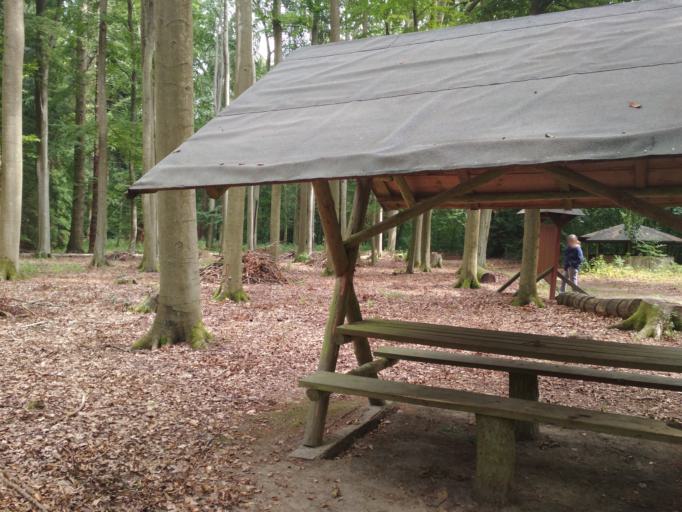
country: DE
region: Mecklenburg-Vorpommern
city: Rechlin
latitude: 53.3206
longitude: 12.8404
